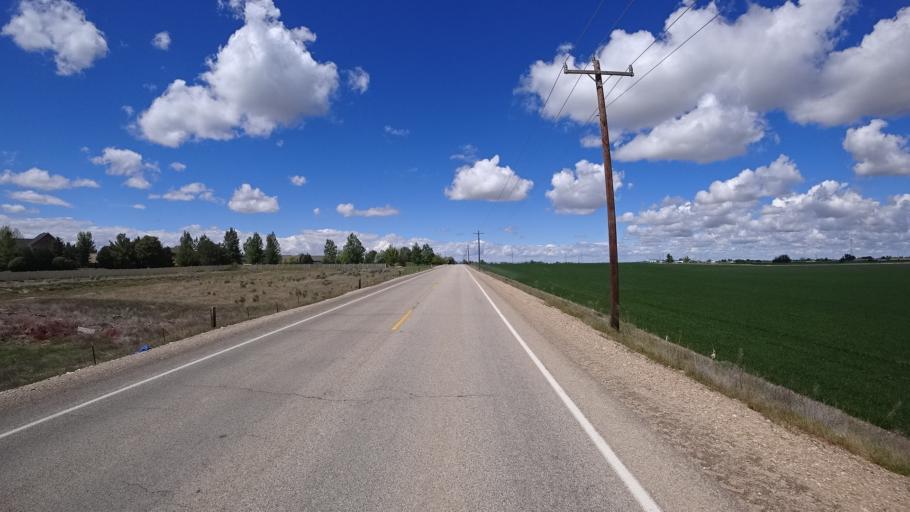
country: US
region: Idaho
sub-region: Ada County
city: Kuna
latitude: 43.4592
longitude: -116.3270
